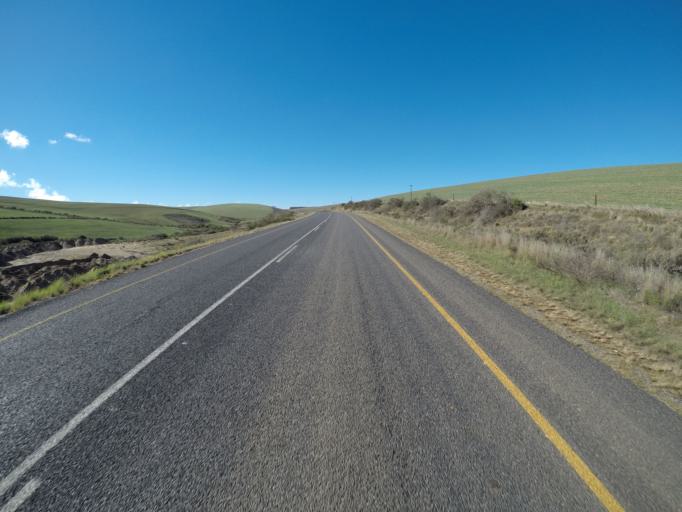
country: ZA
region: Western Cape
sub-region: Overberg District Municipality
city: Caledon
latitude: -34.1508
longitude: 19.4781
